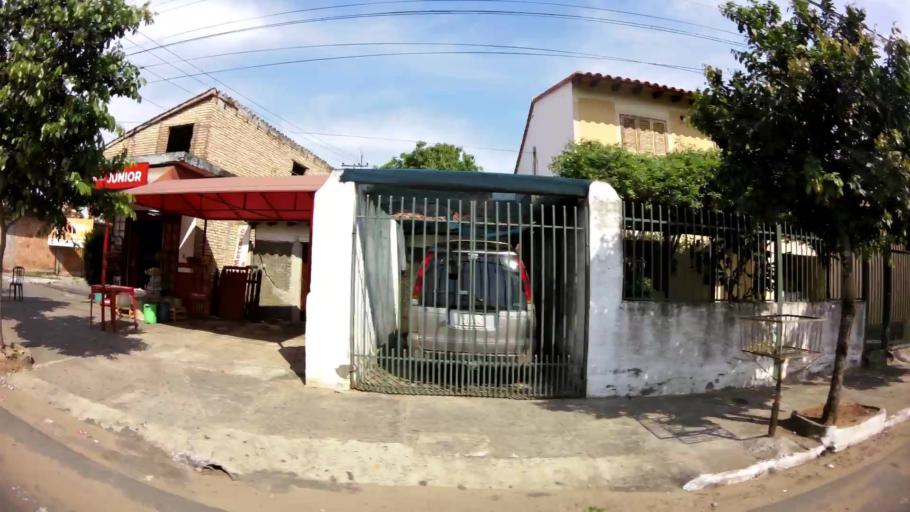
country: PY
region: Central
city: Fernando de la Mora
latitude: -25.2711
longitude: -57.5472
